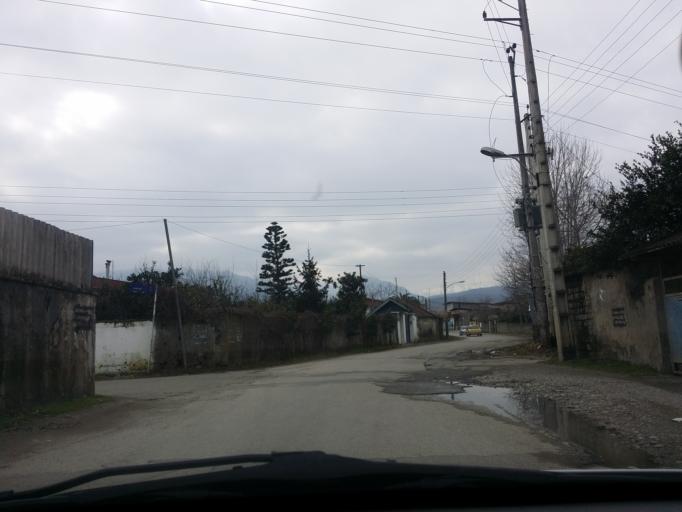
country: IR
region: Mazandaran
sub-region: Nowshahr
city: Nowshahr
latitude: 36.6544
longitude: 51.4769
